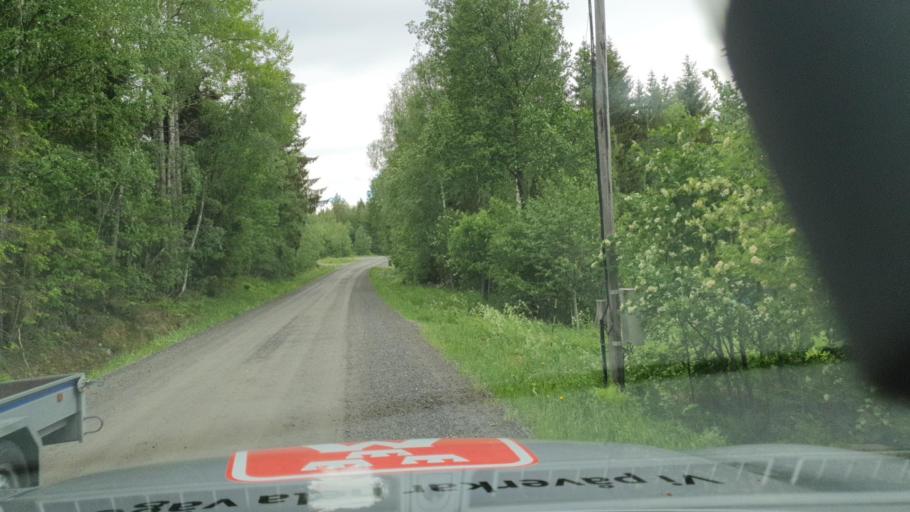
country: SE
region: Vaesternorrland
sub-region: Kramfors Kommun
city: Nordingra
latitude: 62.9984
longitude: 18.2466
